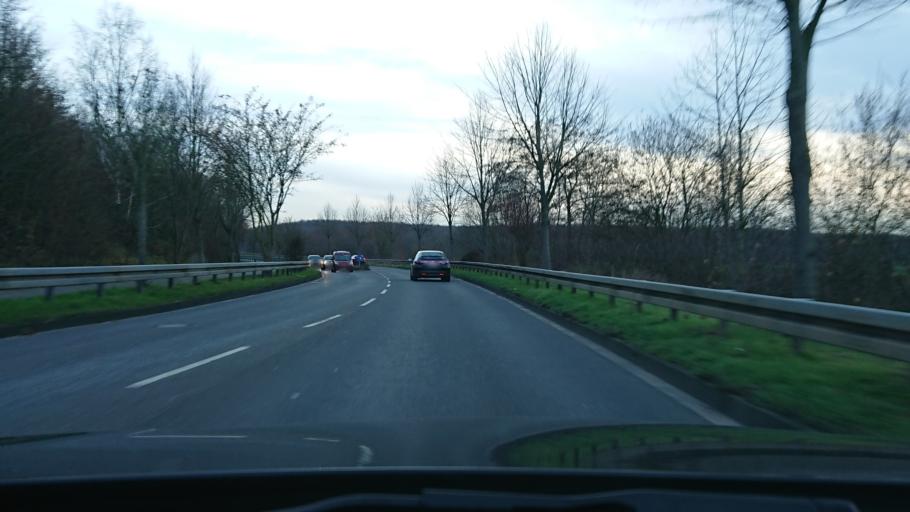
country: DE
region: North Rhine-Westphalia
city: Monheim am Rhein
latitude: 51.0378
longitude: 6.8798
